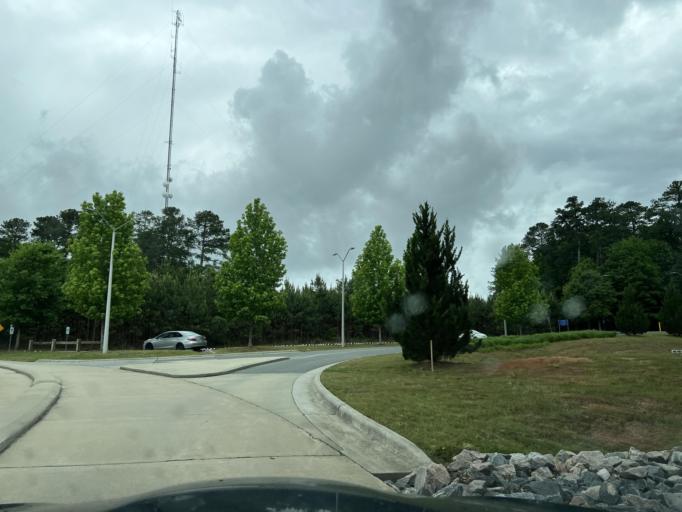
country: US
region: North Carolina
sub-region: Wake County
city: Wake Forest
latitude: 35.9067
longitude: -78.5841
